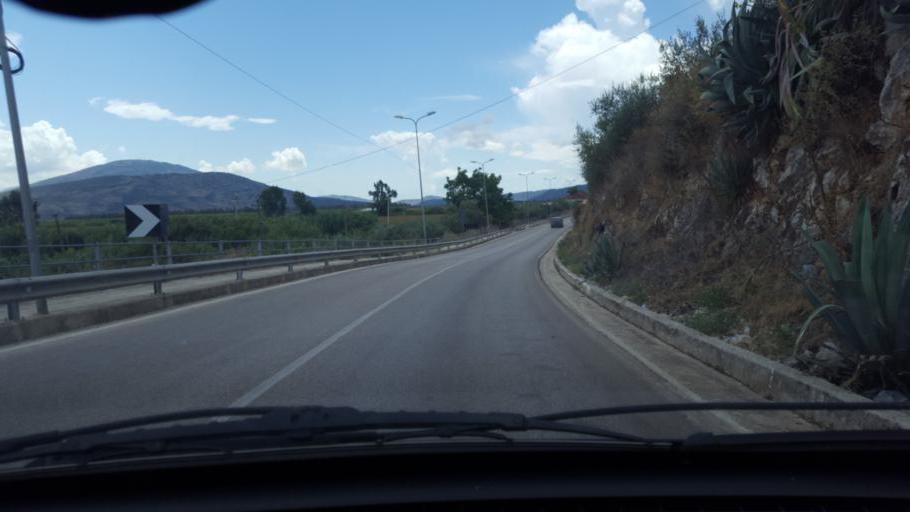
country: AL
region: Vlore
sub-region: Rrethi i Sarandes
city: Sarande
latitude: 39.8378
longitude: 20.0240
